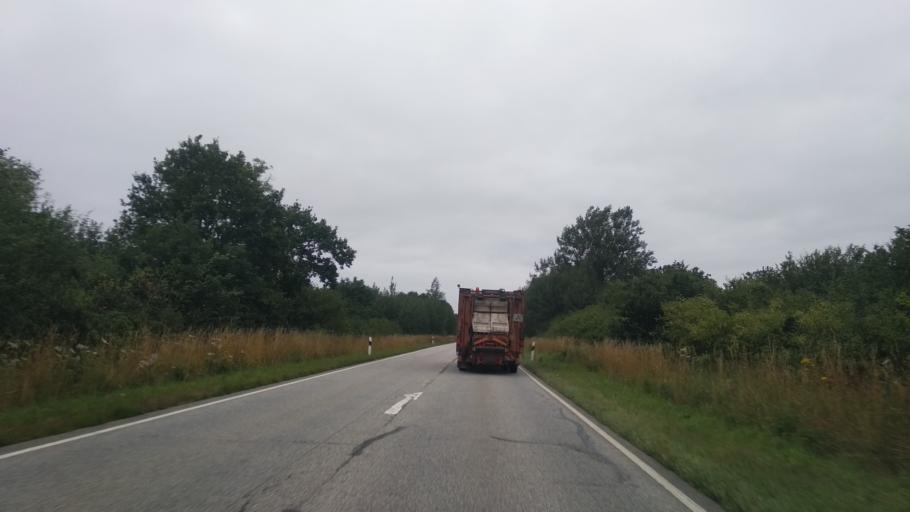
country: DE
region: Schleswig-Holstein
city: Lurschau
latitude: 54.5719
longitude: 9.4796
